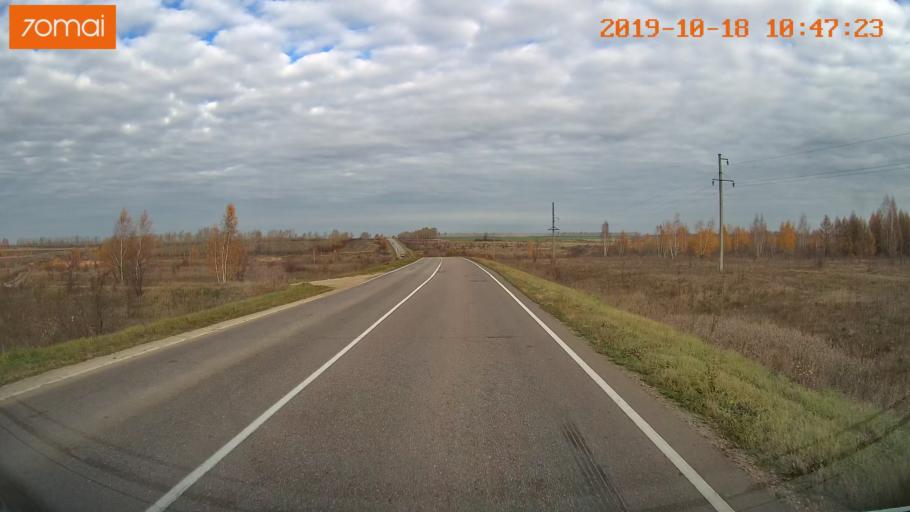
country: RU
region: Tula
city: Yepifan'
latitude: 53.7004
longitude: 38.6978
